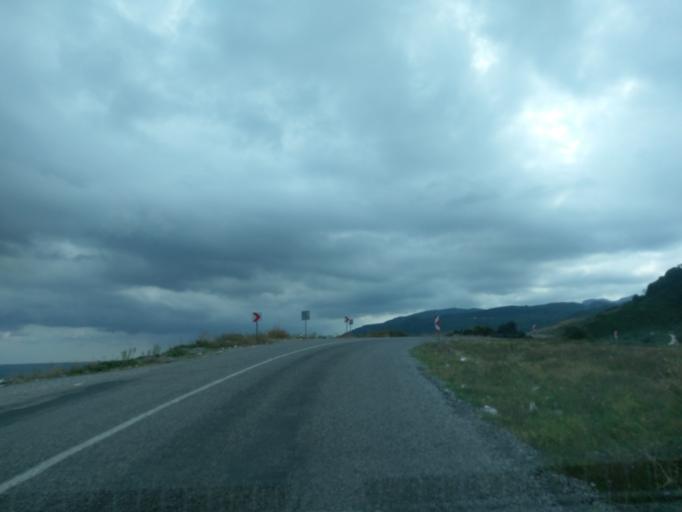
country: TR
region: Sinop
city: Helaldi
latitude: 41.9519
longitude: 34.3768
